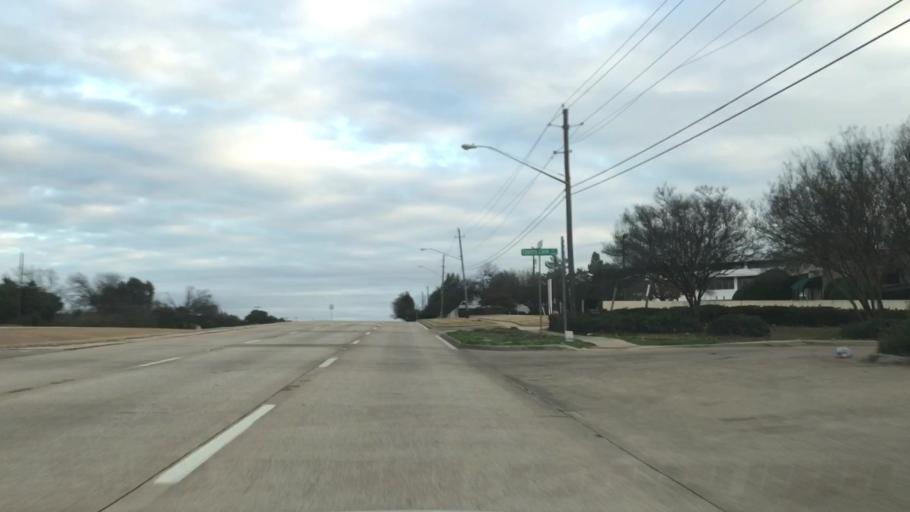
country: US
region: Texas
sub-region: Dallas County
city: Cockrell Hill
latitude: 32.6985
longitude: -96.8977
